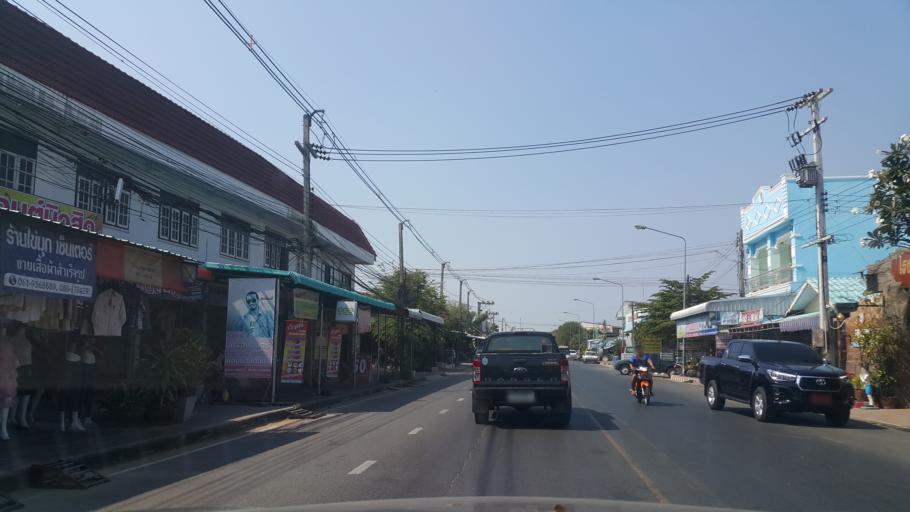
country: TH
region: Buriram
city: Satuek
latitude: 15.2941
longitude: 103.2871
